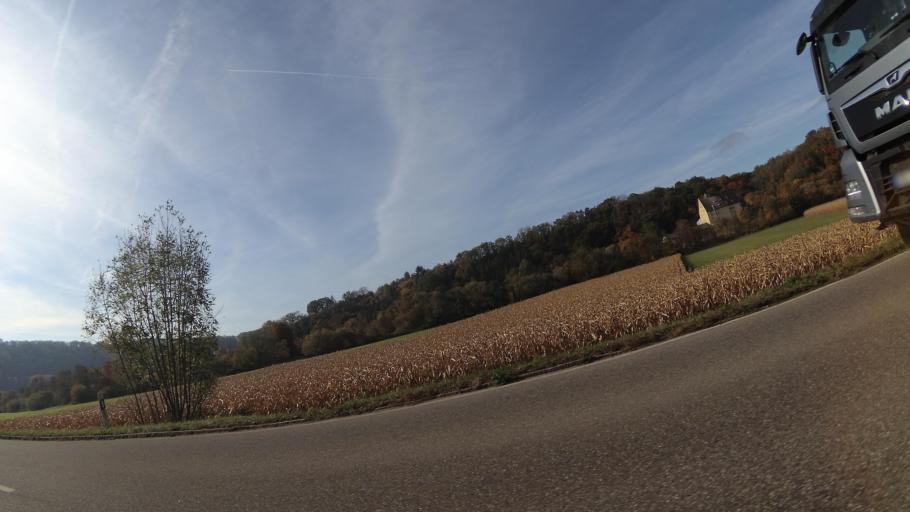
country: DE
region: Baden-Wuerttemberg
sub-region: Regierungsbezirk Stuttgart
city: Mockmuhl
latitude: 49.3119
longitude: 9.3636
